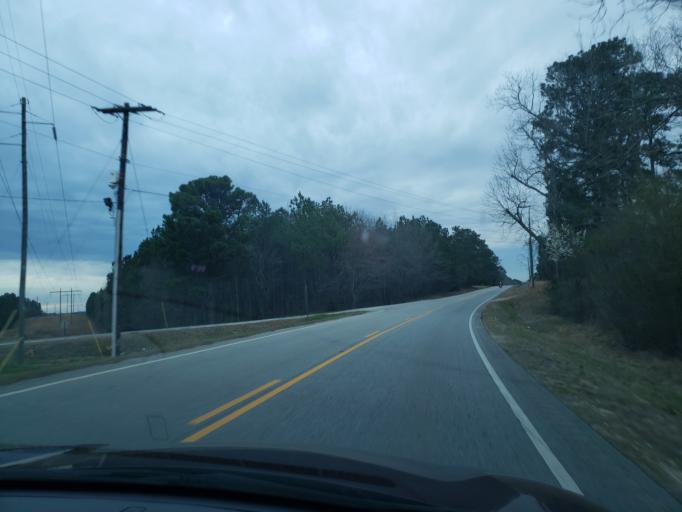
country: US
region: Alabama
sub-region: Chambers County
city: Lafayette
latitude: 33.0061
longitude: -85.3690
